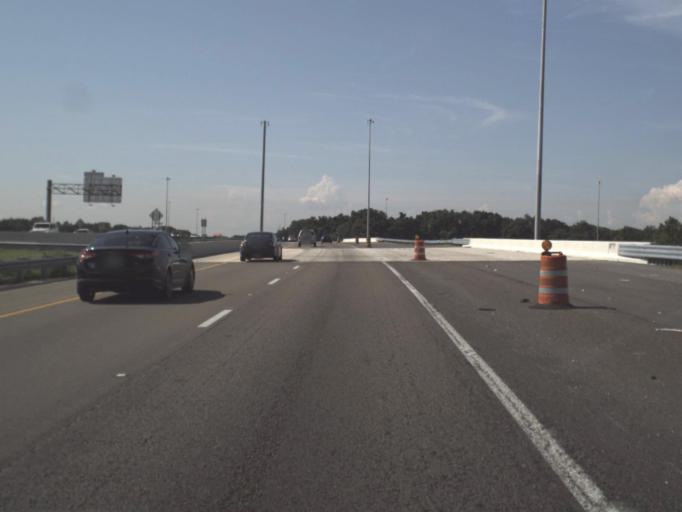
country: US
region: Florida
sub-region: Hillsborough County
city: Temple Terrace
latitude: 28.0564
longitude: -82.3540
